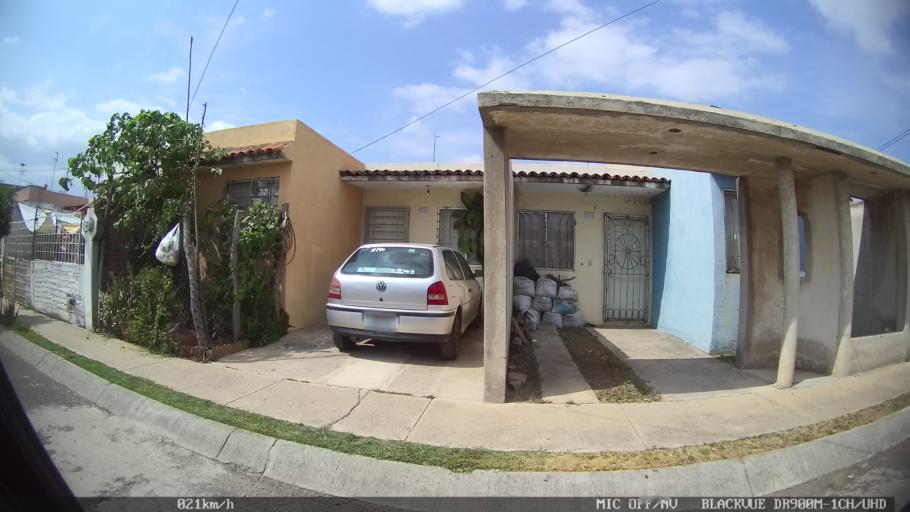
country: MX
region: Jalisco
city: Coyula
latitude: 20.6406
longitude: -103.2173
